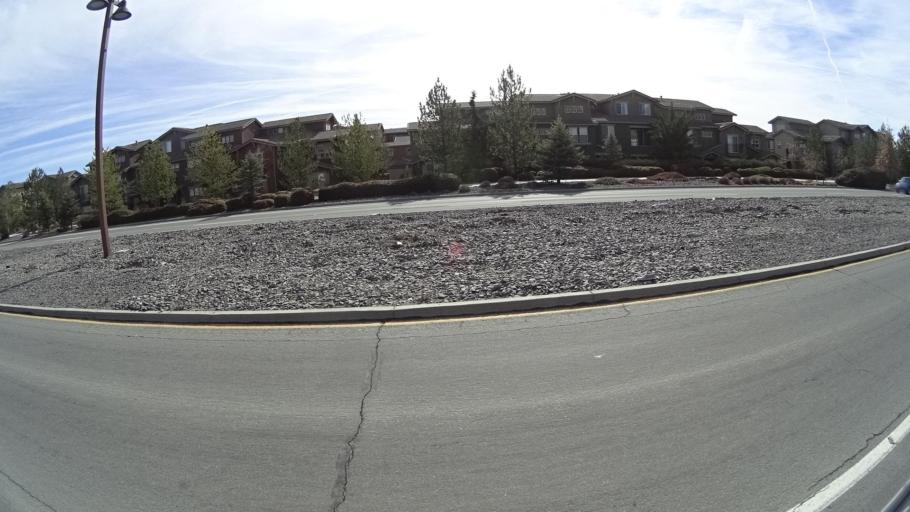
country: US
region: Nevada
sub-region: Washoe County
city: Sun Valley
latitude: 39.5984
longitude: -119.7300
